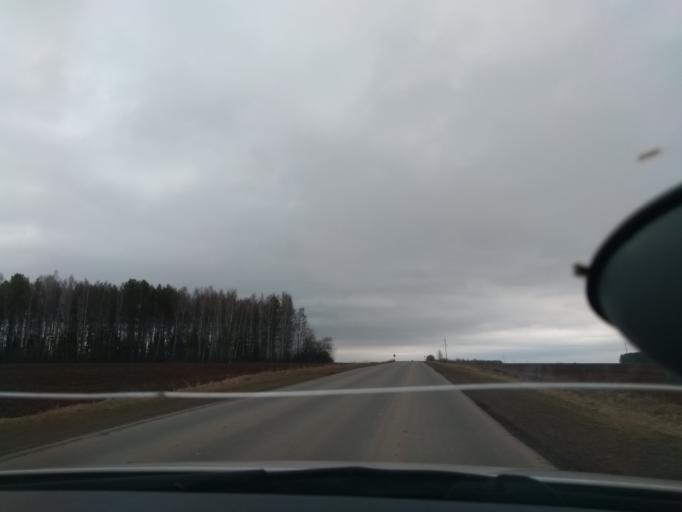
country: RU
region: Perm
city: Kungur
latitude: 57.3741
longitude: 56.8393
